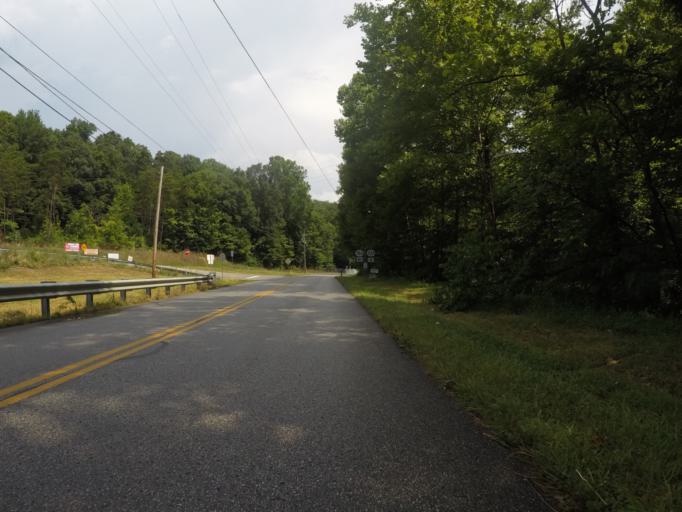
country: US
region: Kentucky
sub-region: Boyd County
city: Ironville
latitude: 38.4510
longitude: -82.6868
